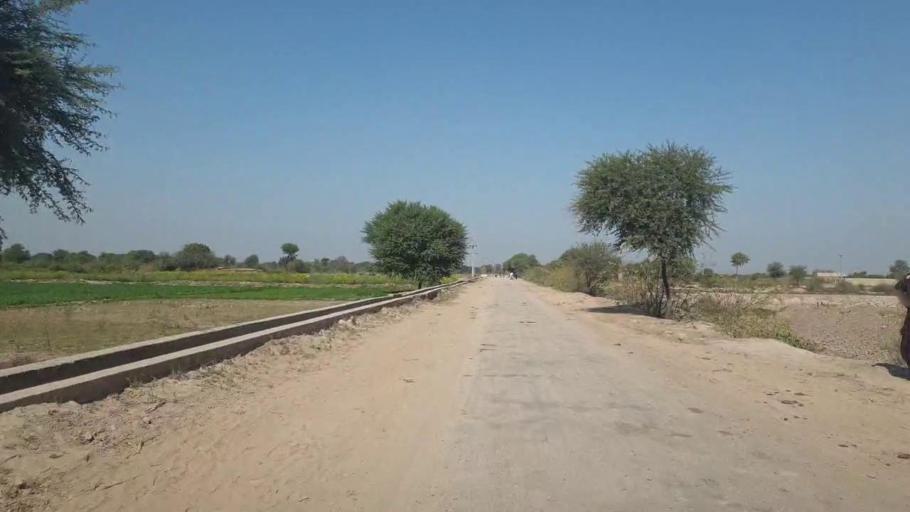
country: PK
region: Sindh
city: Chambar
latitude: 25.2914
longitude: 68.6918
